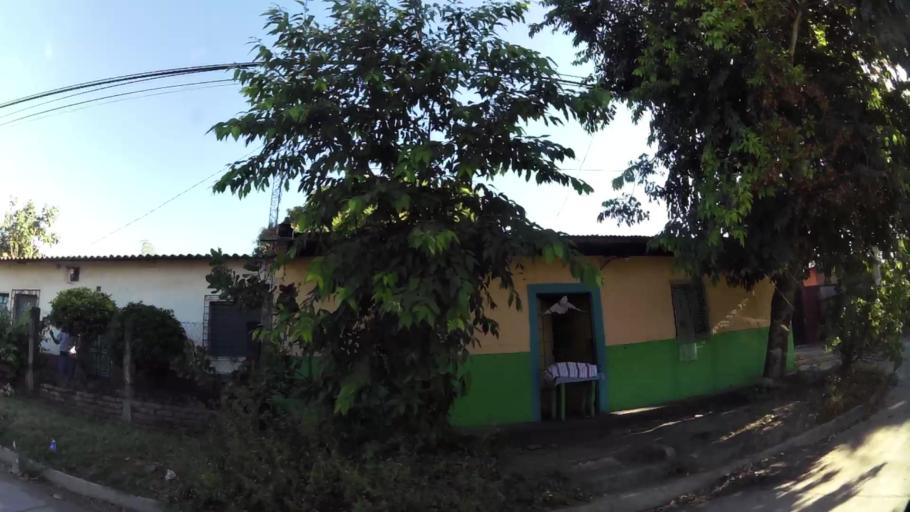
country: SV
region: Sonsonate
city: Sonsonate
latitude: 13.7140
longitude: -89.7157
